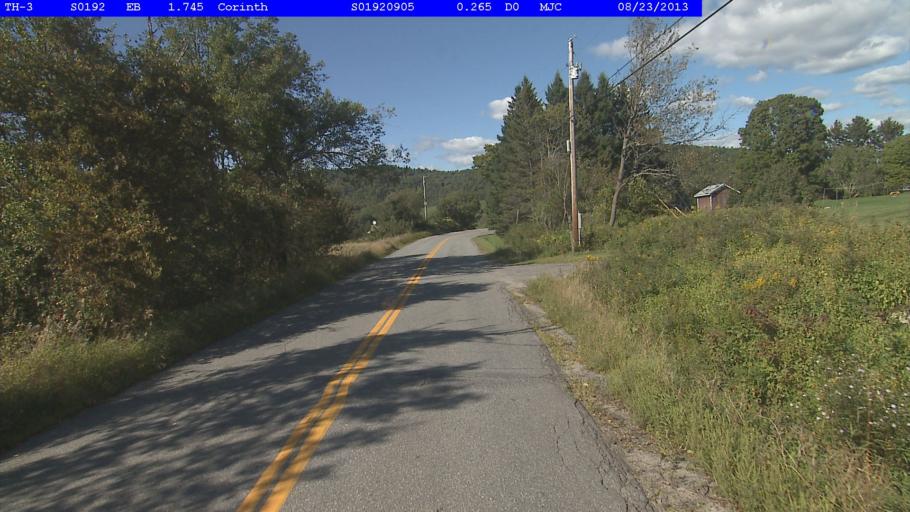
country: US
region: Vermont
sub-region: Orange County
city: Chelsea
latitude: 44.0057
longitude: -72.3505
